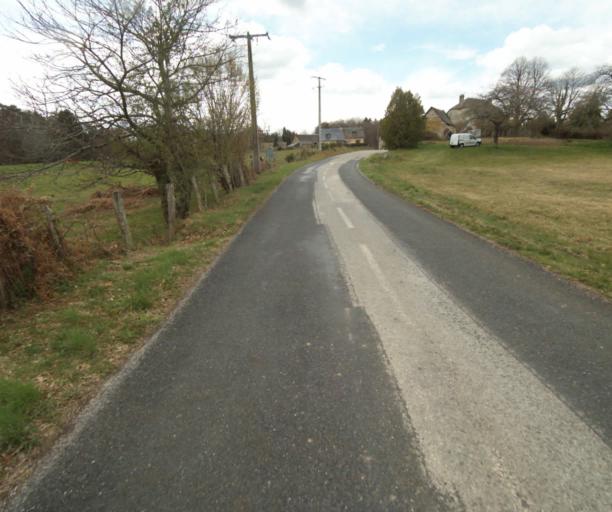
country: FR
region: Limousin
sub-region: Departement de la Correze
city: Argentat
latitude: 45.2115
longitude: 1.9212
